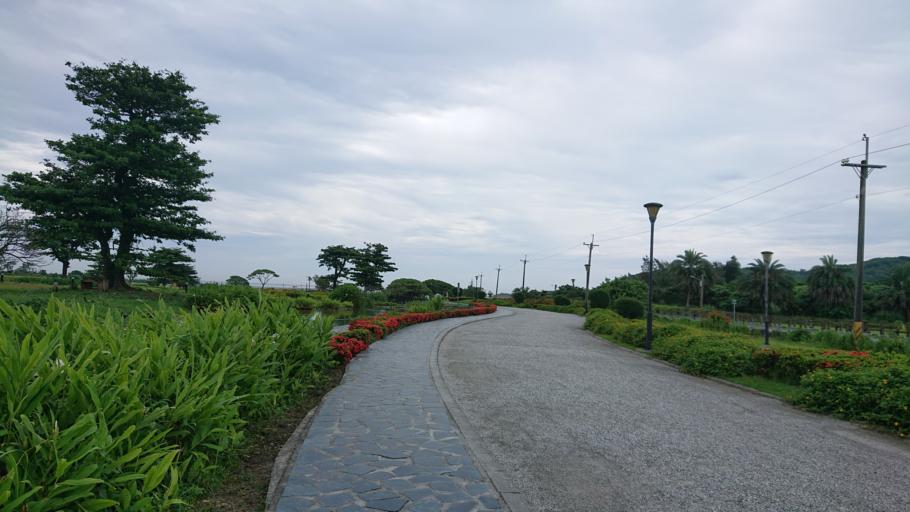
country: TW
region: Taiwan
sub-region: Hualien
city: Hualian
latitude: 23.9372
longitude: 121.5997
